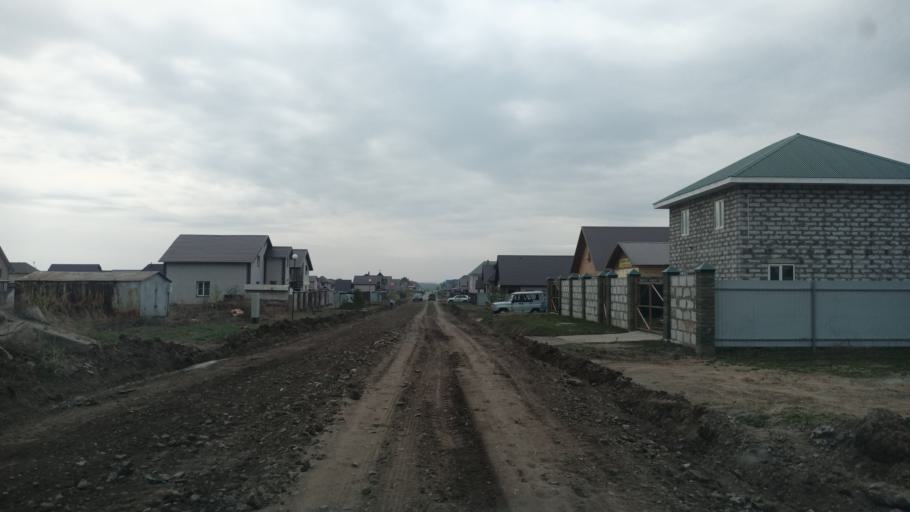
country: RU
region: Altai Krai
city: Yuzhnyy
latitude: 53.2270
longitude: 83.6910
